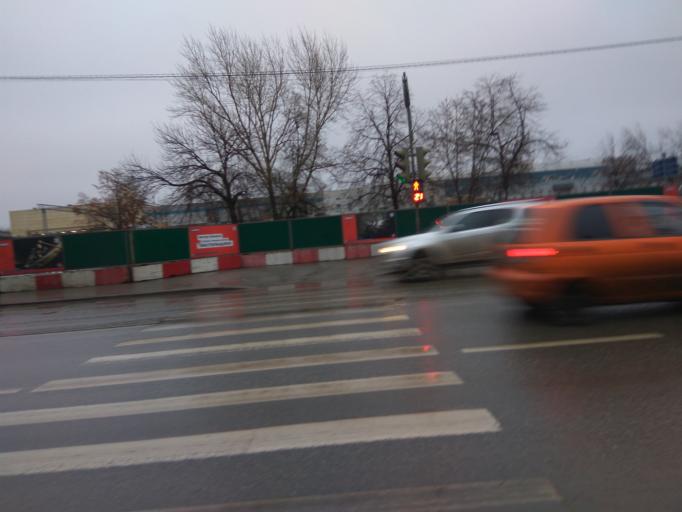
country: RU
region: Moscow
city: Tekstil'shchiki
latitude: 55.7076
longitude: 37.7269
